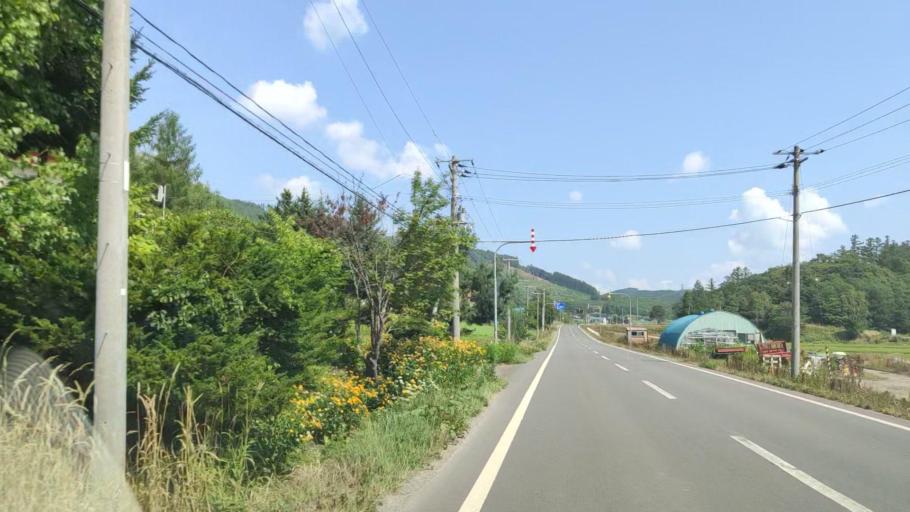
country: JP
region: Hokkaido
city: Shimo-furano
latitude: 43.4324
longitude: 142.4096
